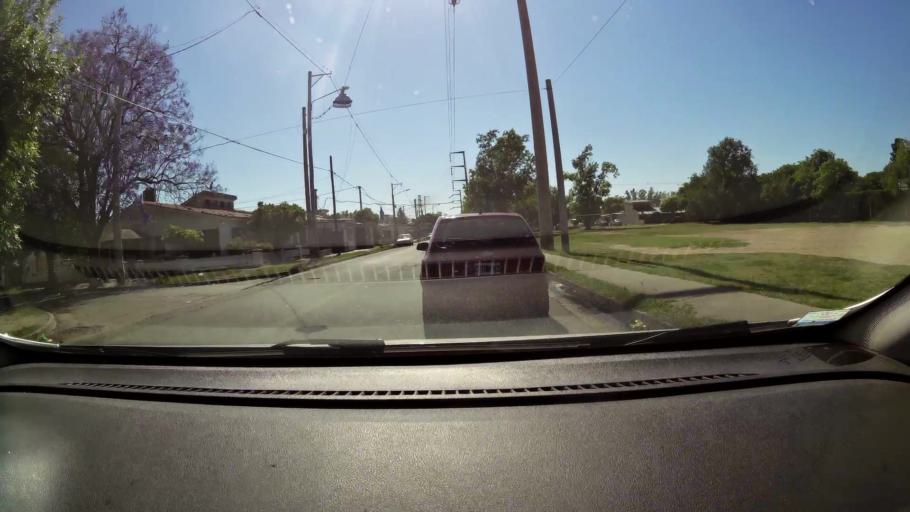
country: AR
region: Cordoba
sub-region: Departamento de Capital
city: Cordoba
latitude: -31.4353
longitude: -64.1386
